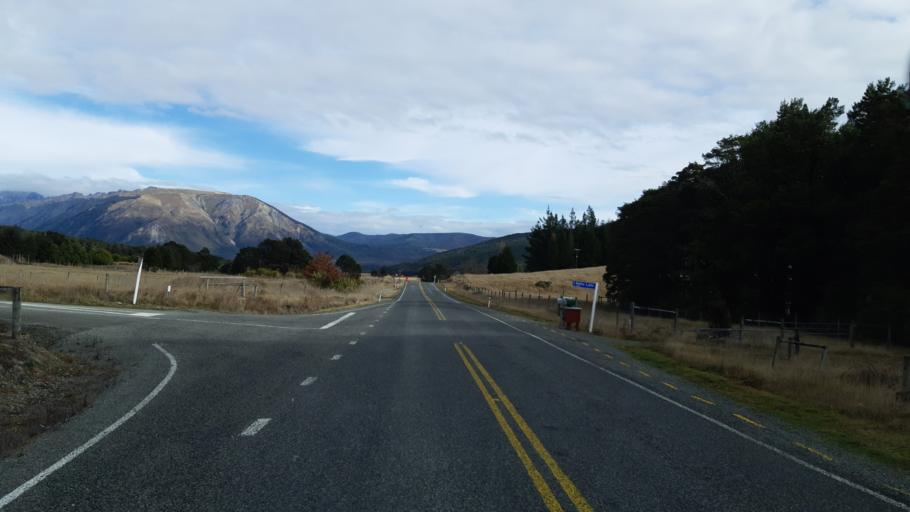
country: NZ
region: Tasman
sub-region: Tasman District
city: Wakefield
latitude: -41.7867
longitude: 172.8896
